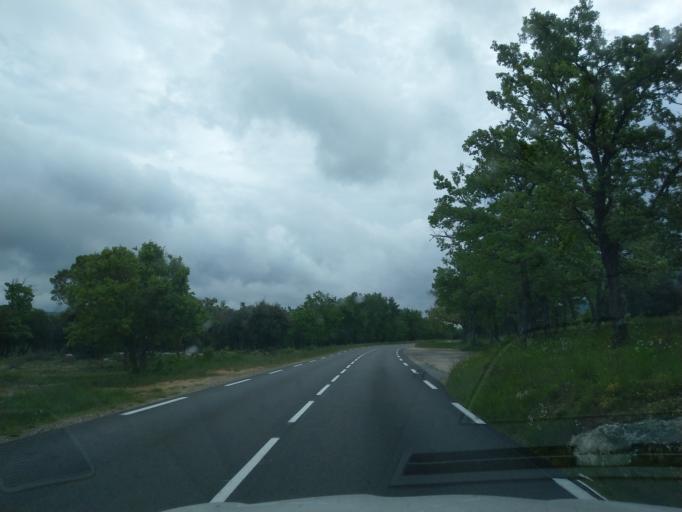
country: FR
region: Provence-Alpes-Cote d'Azur
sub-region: Departement du Var
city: Signes
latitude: 43.2768
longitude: 5.8071
